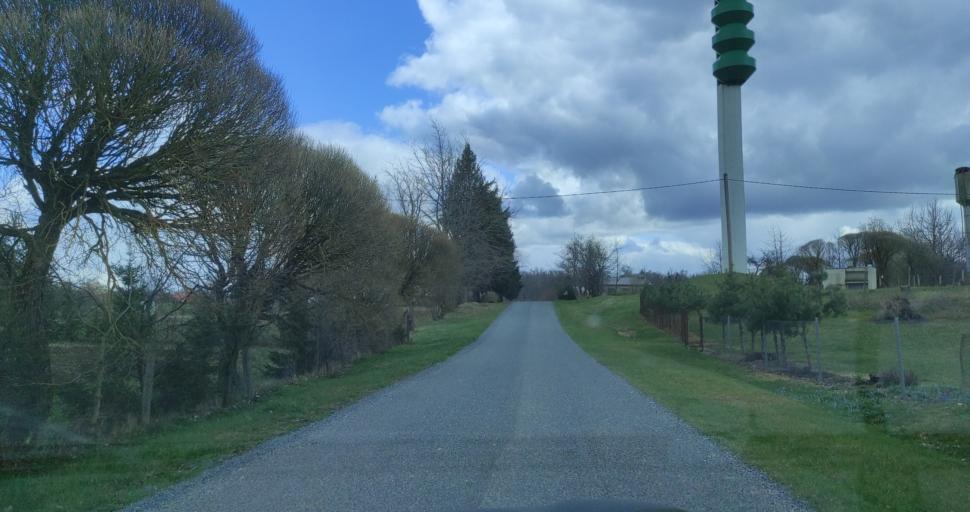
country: LV
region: Aizpute
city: Aizpute
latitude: 56.7130
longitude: 21.5671
